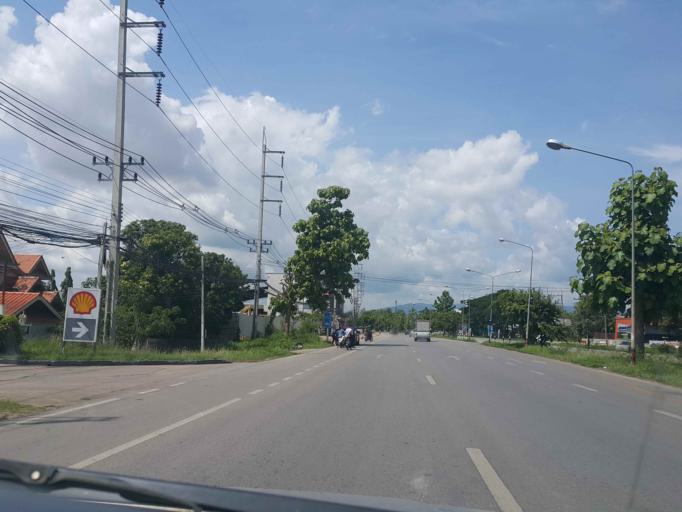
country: TH
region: Phayao
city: Phayao
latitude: 19.1566
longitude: 99.9140
